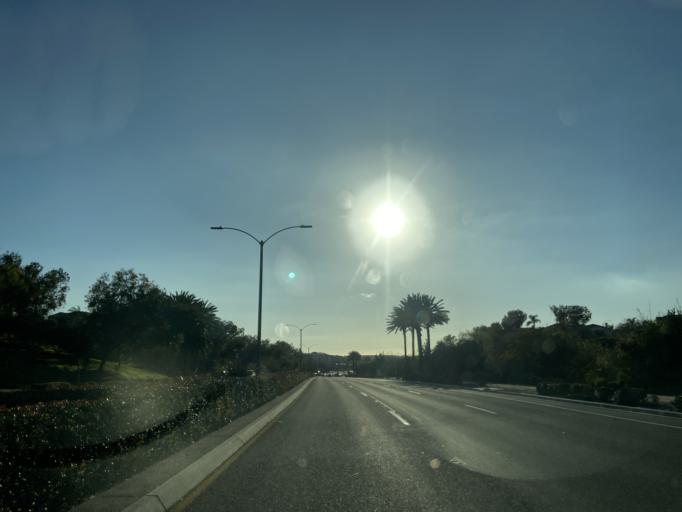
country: US
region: California
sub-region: San Diego County
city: Bonita
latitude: 32.6279
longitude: -116.9819
